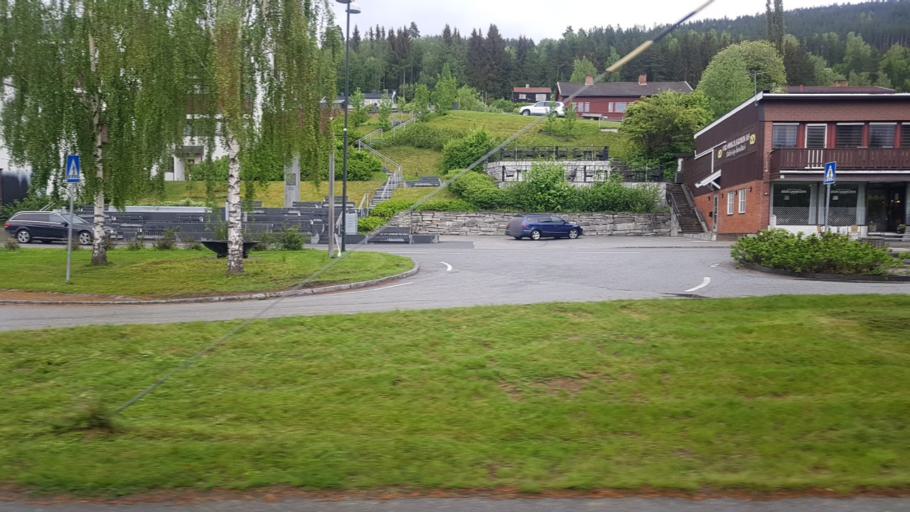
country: NO
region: Oppland
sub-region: Nord-Fron
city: Vinstra
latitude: 61.5976
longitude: 9.7341
